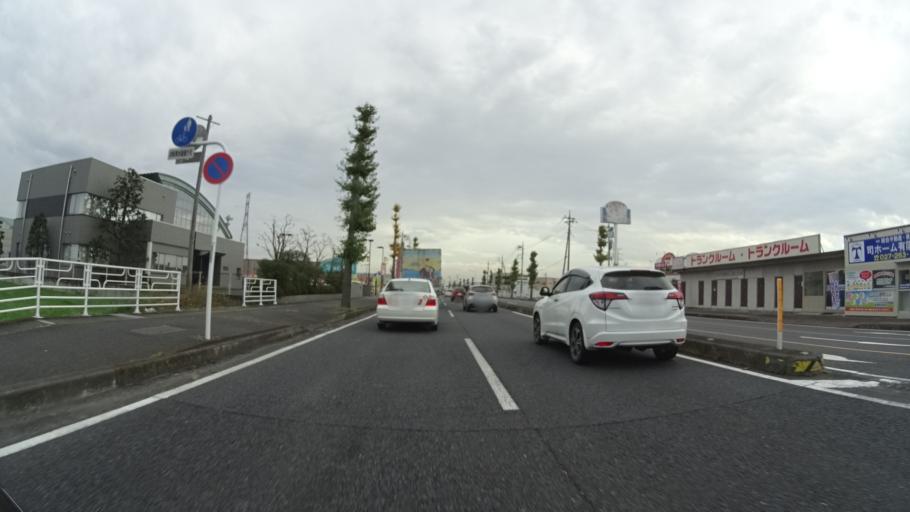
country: JP
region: Gunma
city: Maebashi-shi
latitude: 36.3755
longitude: 139.1205
